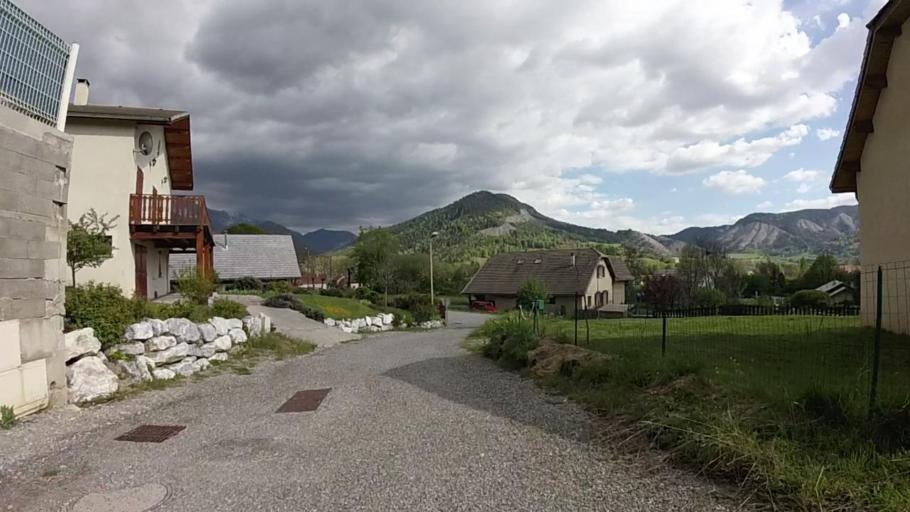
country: FR
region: Provence-Alpes-Cote d'Azur
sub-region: Departement des Alpes-de-Haute-Provence
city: Seyne-les-Alpes
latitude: 44.3493
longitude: 6.3605
